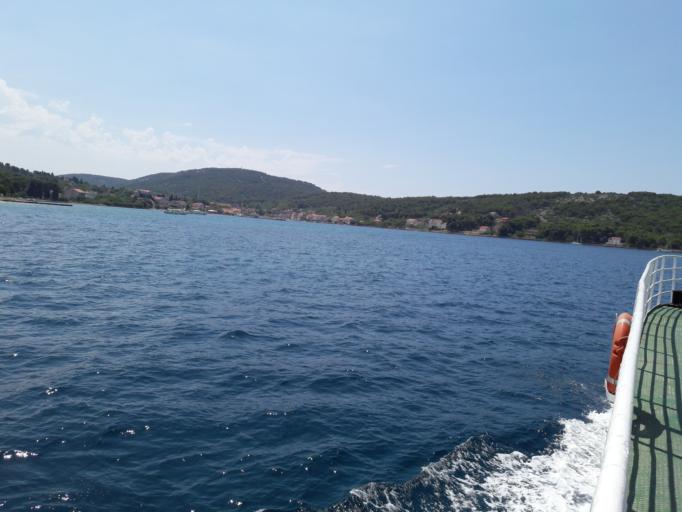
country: HR
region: Sibensko-Kniniska
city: Vodice
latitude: 43.7057
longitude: 15.8306
